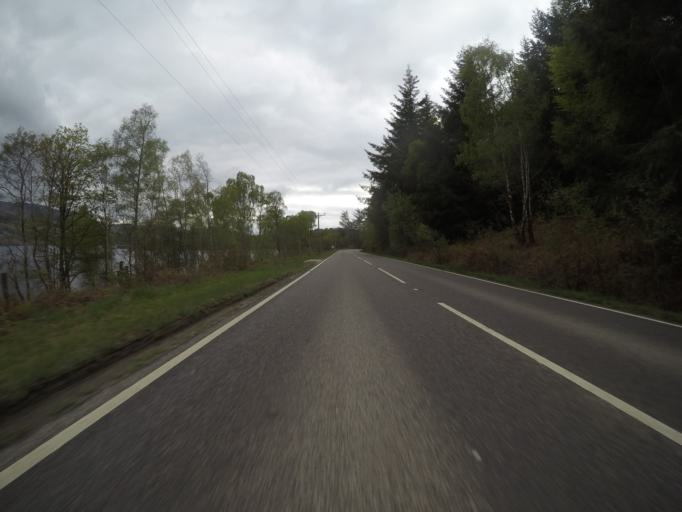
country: GB
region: Scotland
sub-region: Highland
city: Spean Bridge
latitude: 57.1563
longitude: -4.6700
